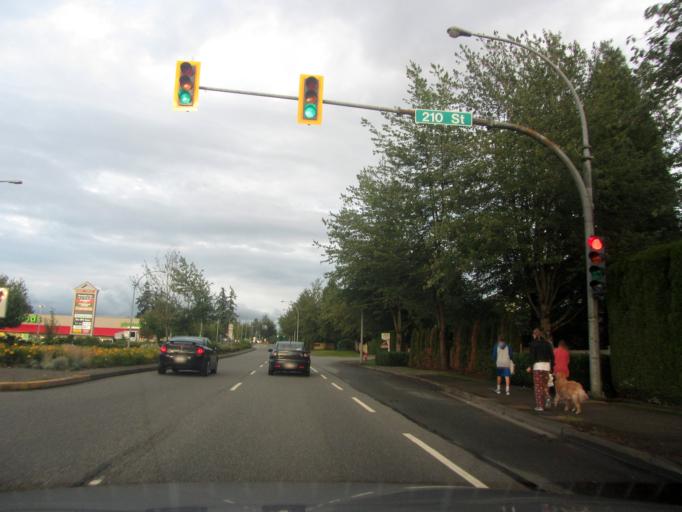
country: CA
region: British Columbia
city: Walnut Grove
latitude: 49.1623
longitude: -122.6376
